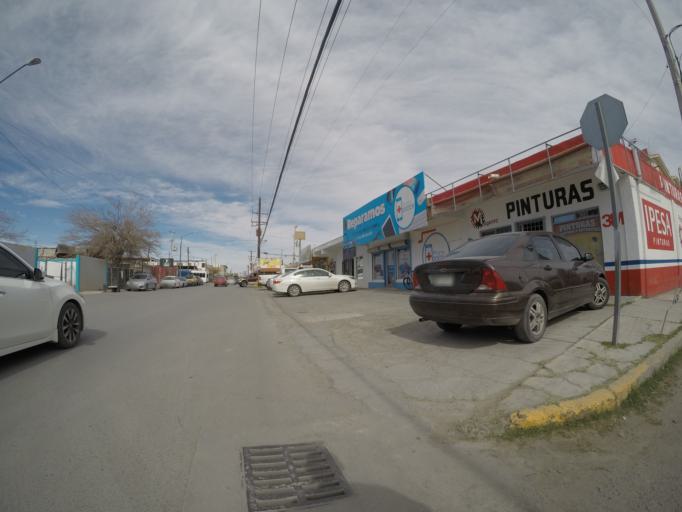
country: MX
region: Chihuahua
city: Ciudad Juarez
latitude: 31.7170
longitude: -106.4324
